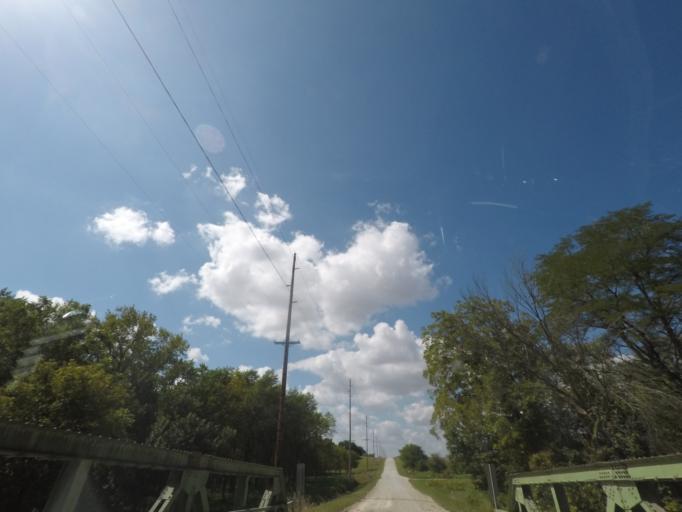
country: US
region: Iowa
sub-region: Story County
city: Nevada
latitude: 42.0343
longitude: -93.3742
